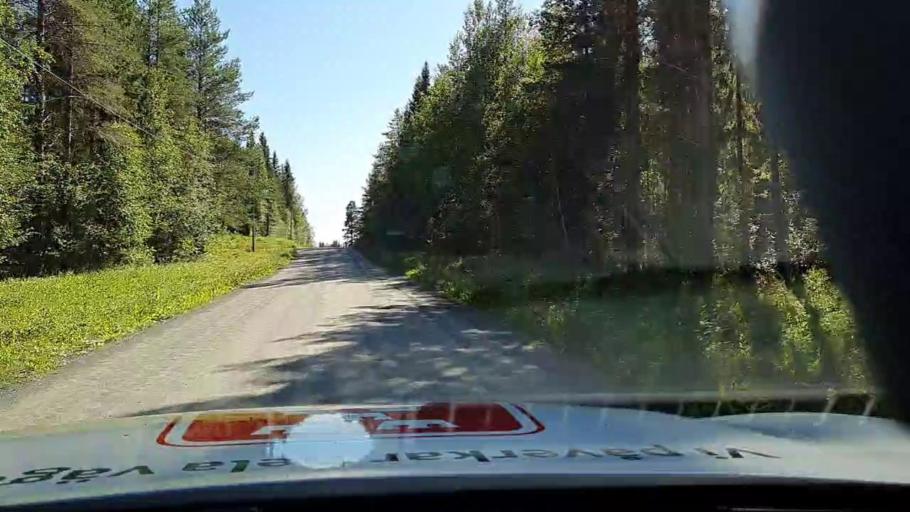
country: SE
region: Jaemtland
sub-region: Krokoms Kommun
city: Krokom
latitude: 63.6867
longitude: 14.6047
